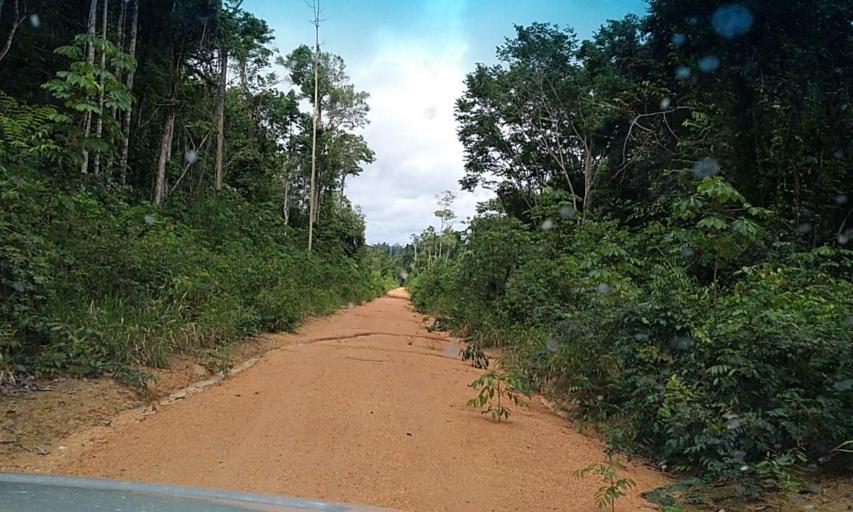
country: BR
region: Para
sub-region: Senador Jose Porfirio
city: Senador Jose Porfirio
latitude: -3.0420
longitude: -51.7225
